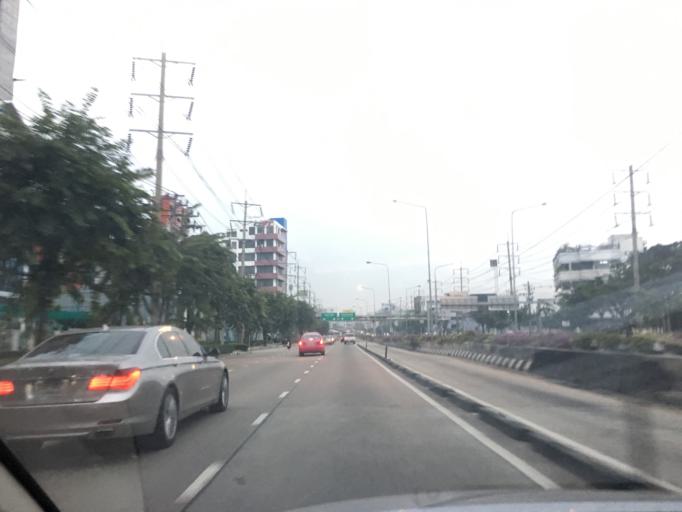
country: TH
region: Bangkok
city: Rat Burana
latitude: 13.6882
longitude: 100.5154
